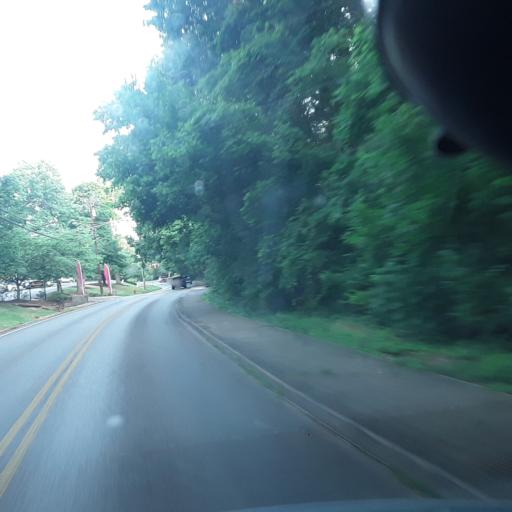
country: US
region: Tennessee
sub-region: Williamson County
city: Brentwood
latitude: 36.0541
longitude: -86.7401
